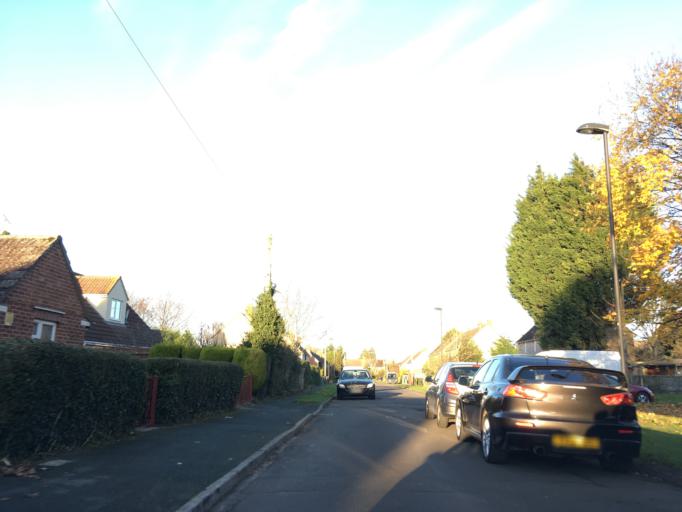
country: GB
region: England
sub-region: South Gloucestershire
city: Thornbury
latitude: 51.6140
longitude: -2.5179
